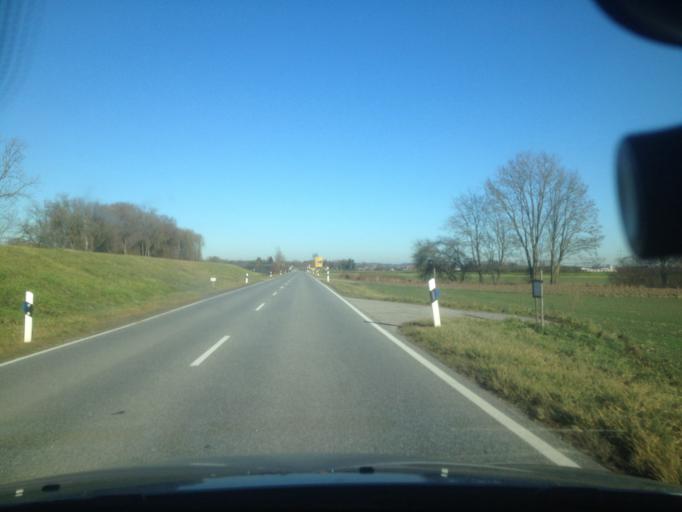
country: DE
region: Bavaria
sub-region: Upper Bavaria
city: Moosburg
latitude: 48.4548
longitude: 11.9489
